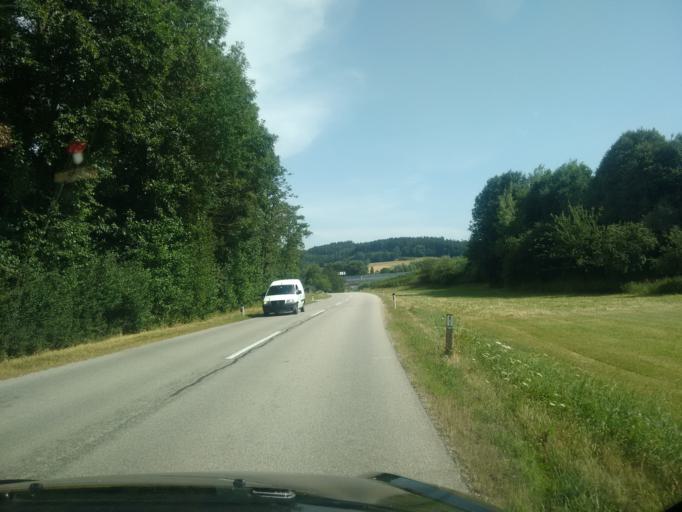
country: AT
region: Upper Austria
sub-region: Wels-Land
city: Offenhausen
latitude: 48.1822
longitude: 13.8567
